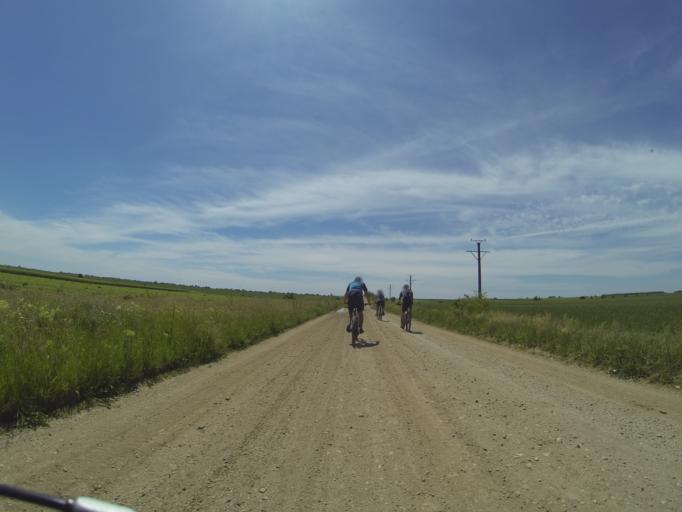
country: RO
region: Dolj
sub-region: Comuna Leu
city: Zanoaga
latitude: 44.1735
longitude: 24.0920
